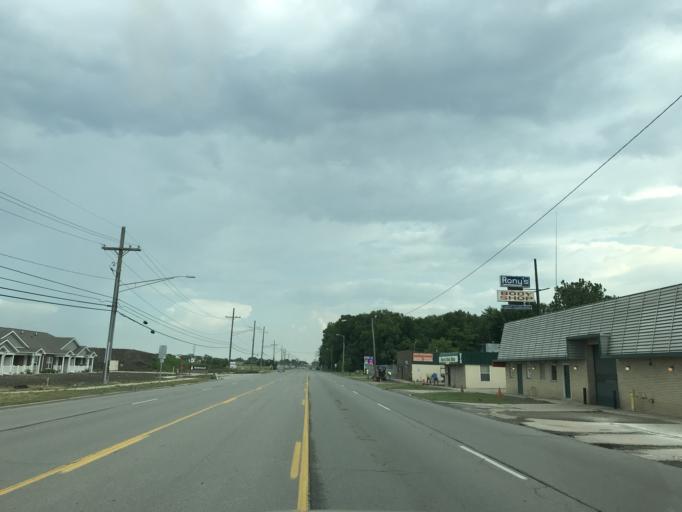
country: US
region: Michigan
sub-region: Wayne County
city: Southgate
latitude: 42.2223
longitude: -83.2296
